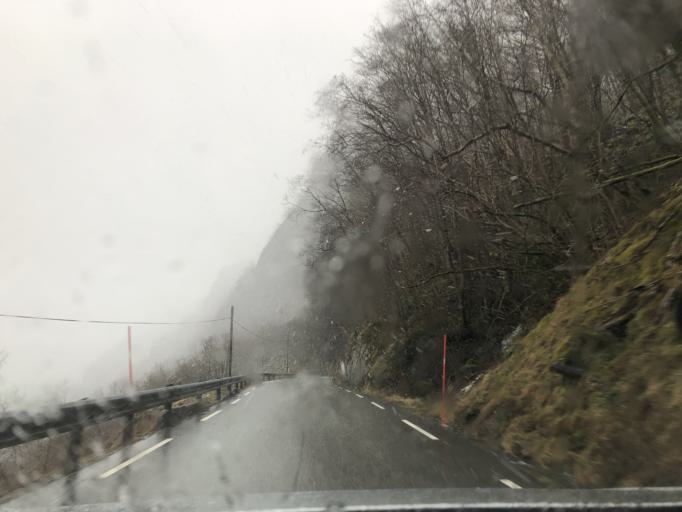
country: NO
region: Rogaland
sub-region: Suldal
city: Sand
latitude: 59.4089
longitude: 6.2123
